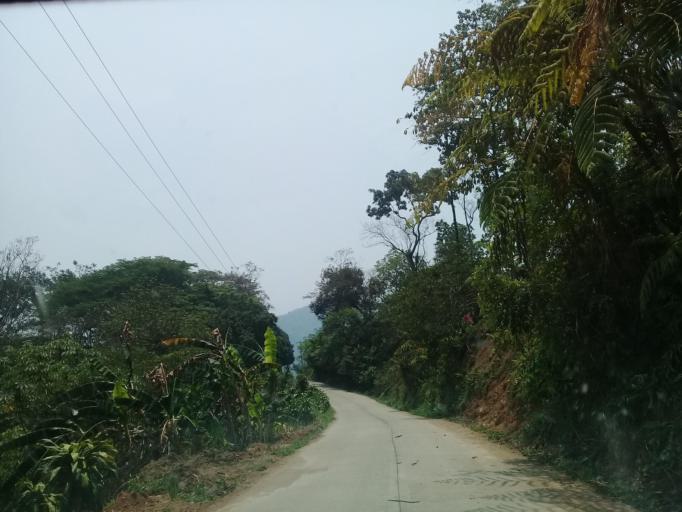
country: MX
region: Veracruz
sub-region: Tezonapa
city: Laguna Chica (Pueblo Nuevo)
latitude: 18.5703
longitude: -96.7300
